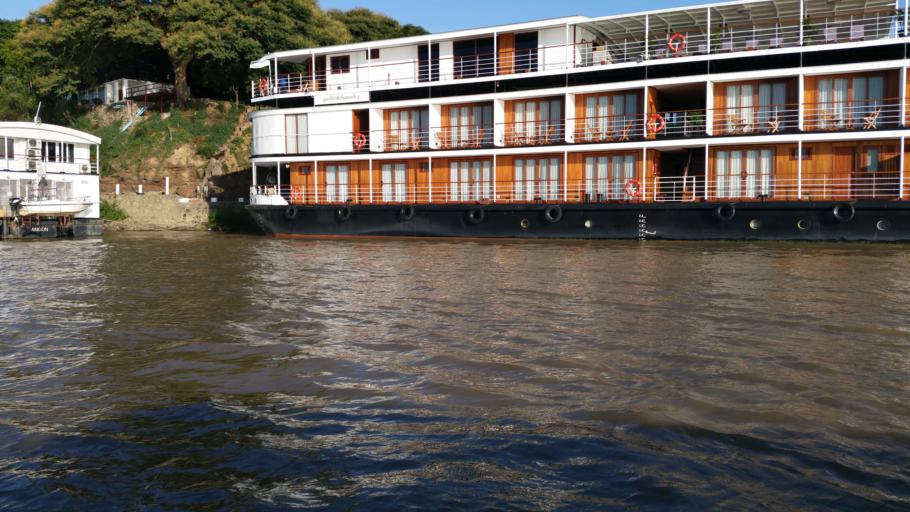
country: MM
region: Magway
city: Pakokku
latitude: 21.1804
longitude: 94.8610
